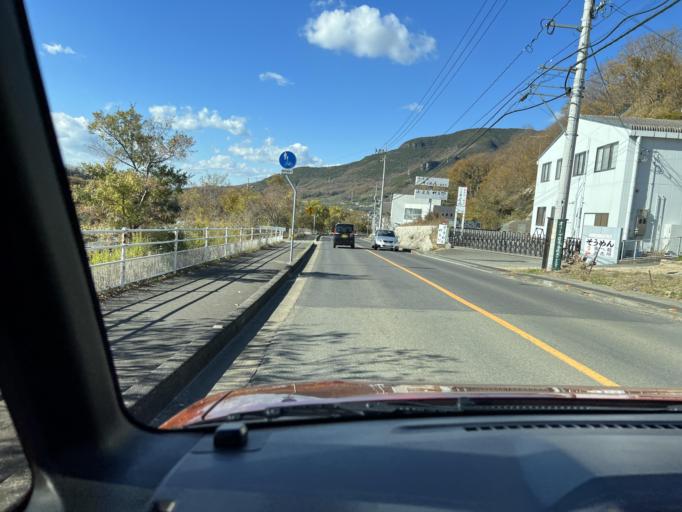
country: JP
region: Kagawa
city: Tonosho
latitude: 34.4809
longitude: 134.2456
